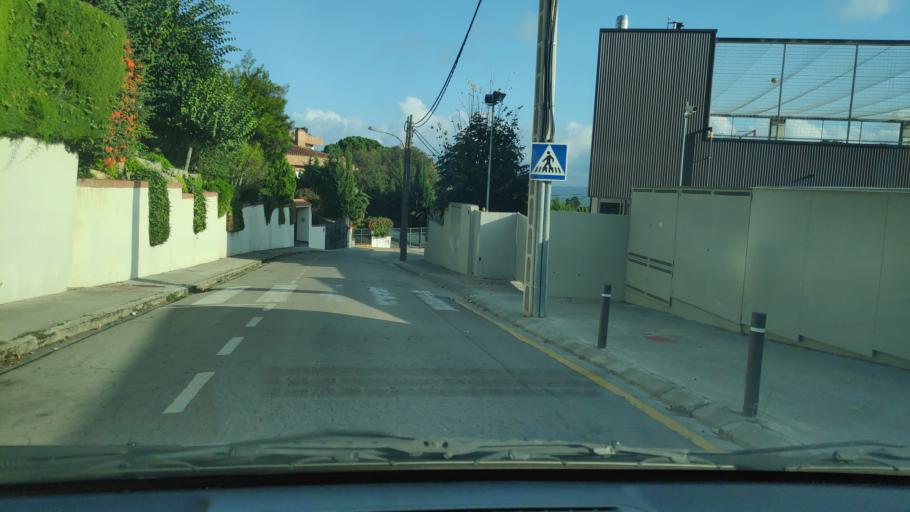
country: ES
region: Catalonia
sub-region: Provincia de Barcelona
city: Sant Quirze del Valles
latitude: 41.5037
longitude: 2.0837
